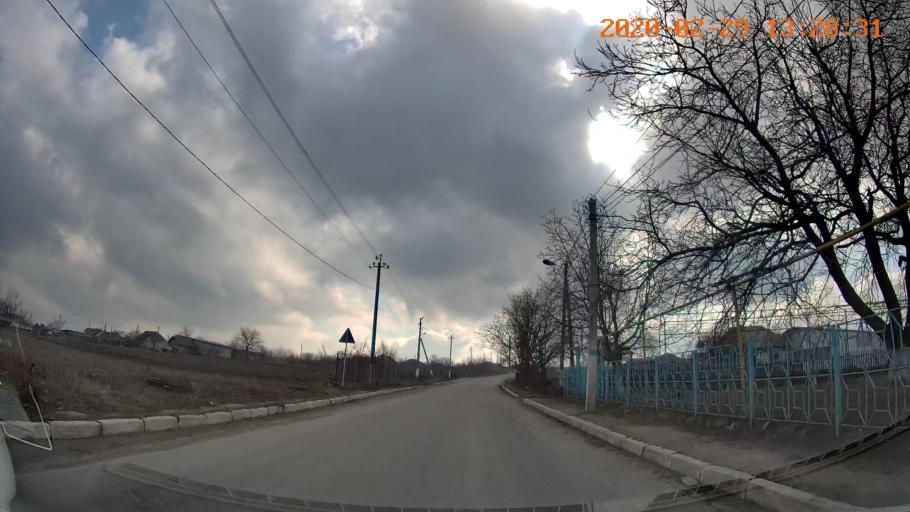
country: MD
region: Telenesti
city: Camenca
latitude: 47.9046
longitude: 28.6422
